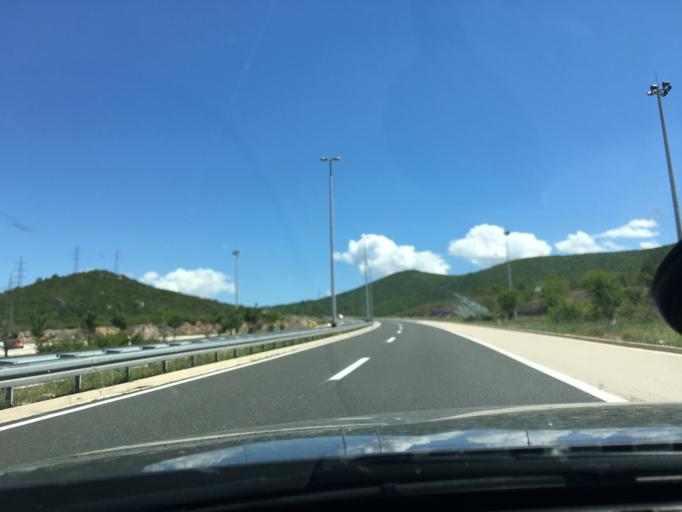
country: HR
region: Splitsko-Dalmatinska
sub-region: Grad Trogir
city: Trogir
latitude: 43.6667
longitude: 16.1673
